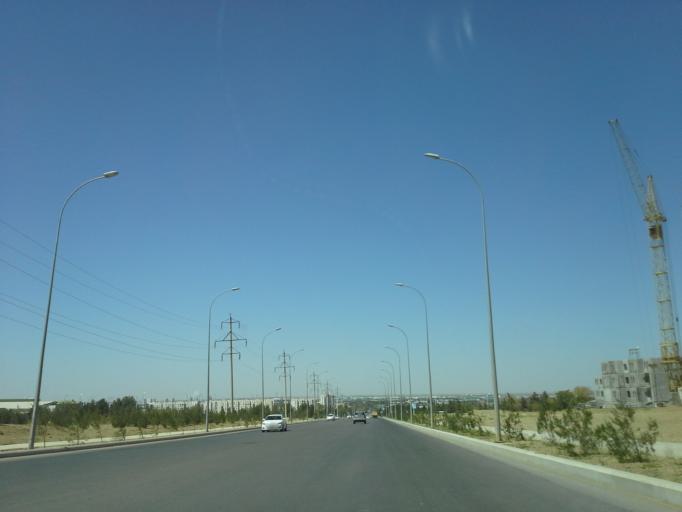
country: TM
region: Ahal
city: Ashgabat
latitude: 37.8969
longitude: 58.4057
